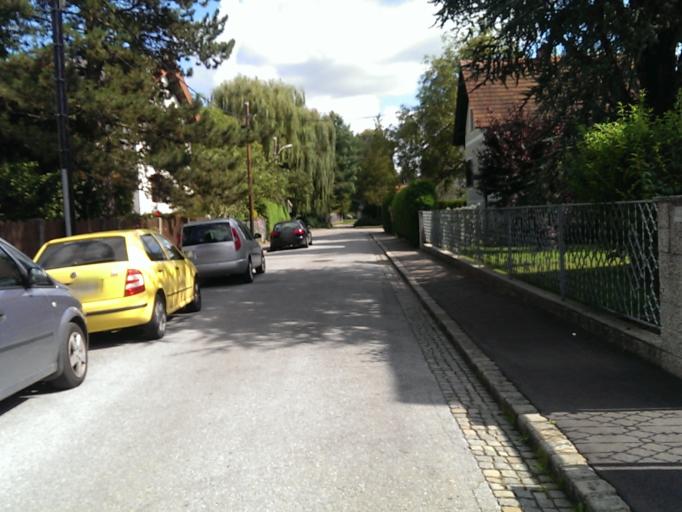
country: AT
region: Styria
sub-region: Graz Stadt
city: Graz
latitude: 47.0553
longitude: 15.4626
